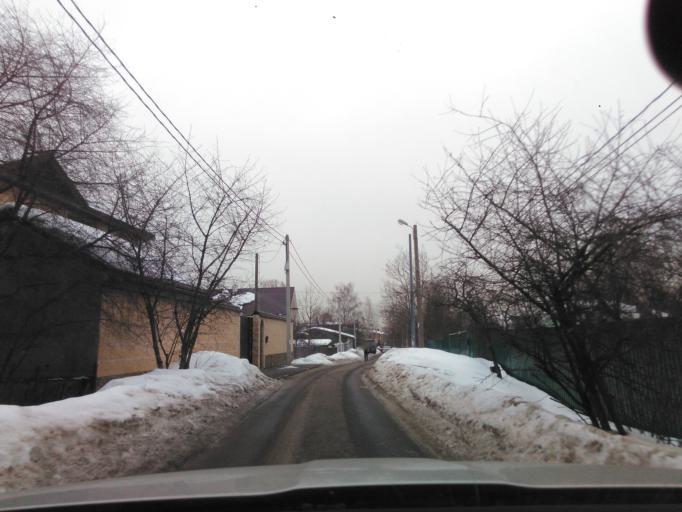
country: RU
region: Moscow
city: Khimki
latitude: 55.8882
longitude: 37.3890
